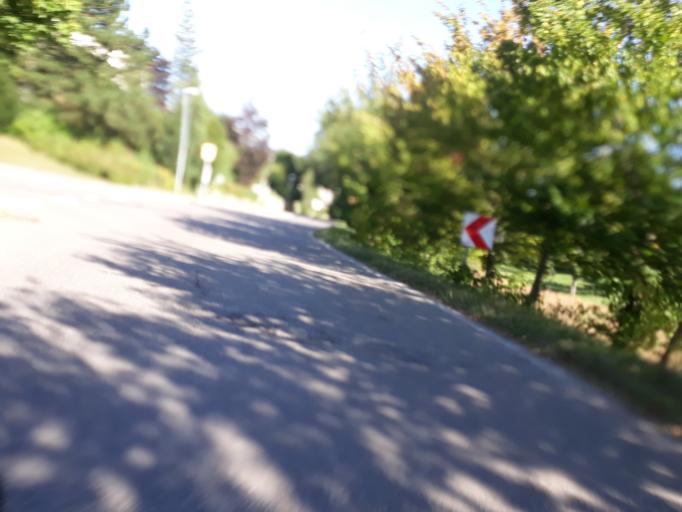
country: DE
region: Baden-Wuerttemberg
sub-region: Karlsruhe Region
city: Gechingen
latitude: 48.6831
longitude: 8.8481
